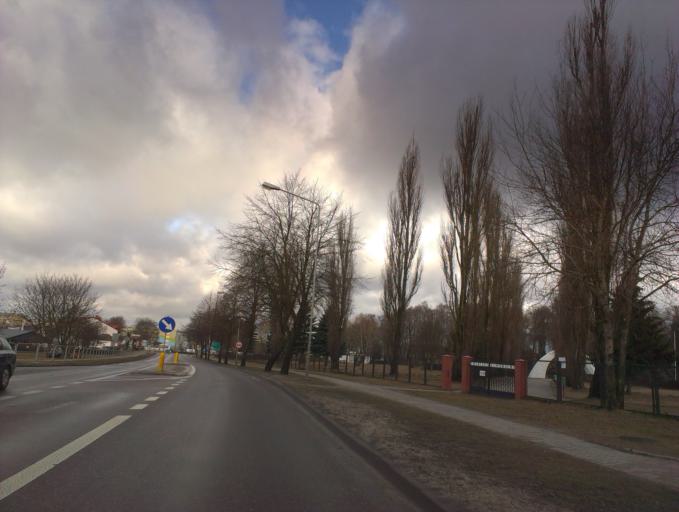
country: PL
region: West Pomeranian Voivodeship
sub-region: Powiat szczecinecki
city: Szczecinek
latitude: 53.7094
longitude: 16.7080
